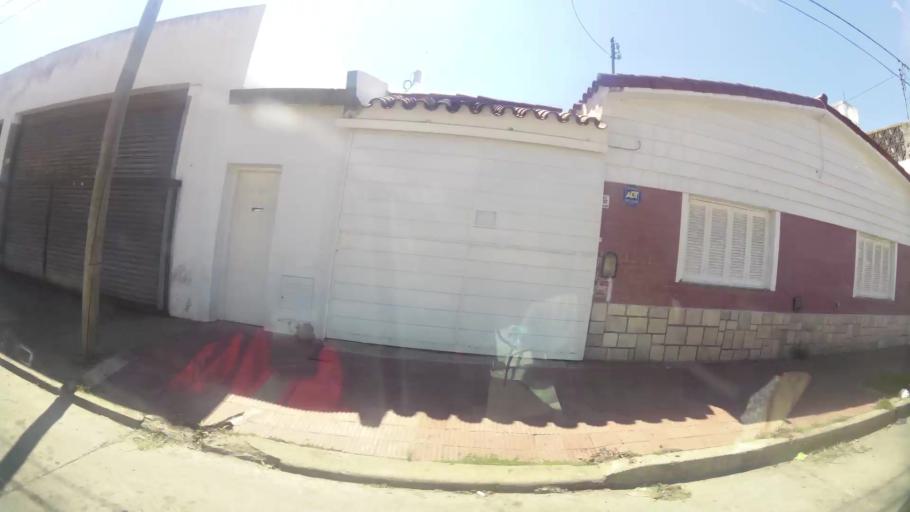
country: AR
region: Cordoba
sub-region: Departamento de Capital
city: Cordoba
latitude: -31.4164
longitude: -64.2128
